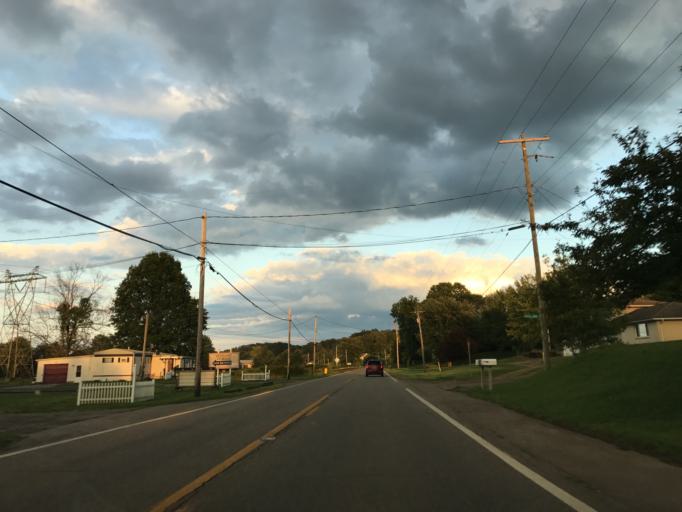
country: US
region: Ohio
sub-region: Stark County
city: Minerva
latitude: 40.7474
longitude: -81.0684
